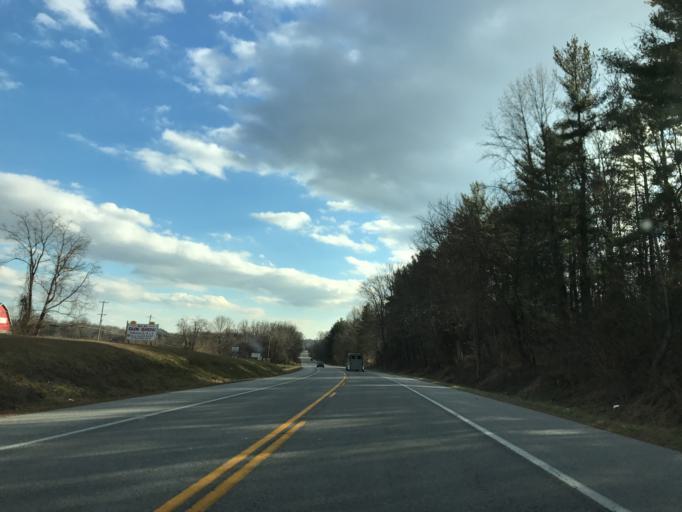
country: US
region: Maryland
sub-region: Cecil County
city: Rising Sun
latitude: 39.6648
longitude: -76.0759
